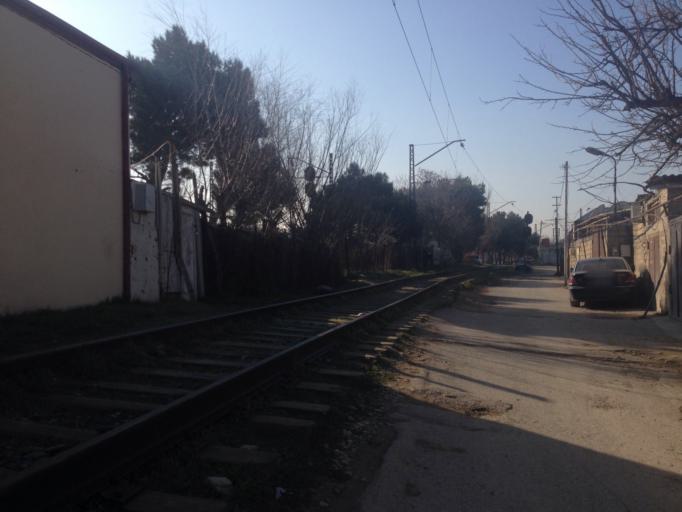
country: AZ
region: Baki
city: Baku
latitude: 40.3920
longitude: 49.8838
